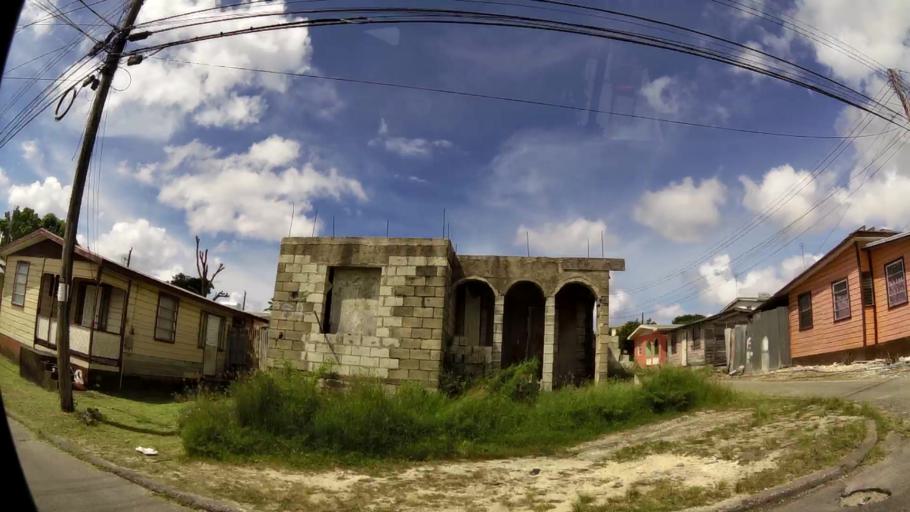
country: BB
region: Saint Michael
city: Bridgetown
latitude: 13.1343
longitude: -59.6214
